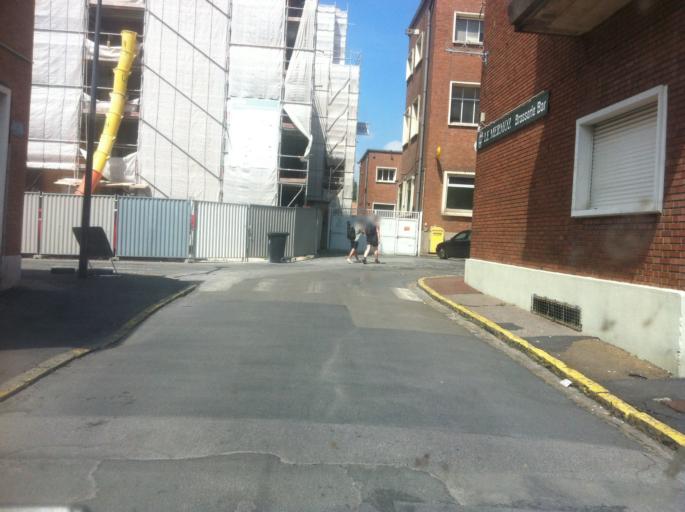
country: FR
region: Nord-Pas-de-Calais
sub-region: Departement du Nord
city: Maubeuge
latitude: 50.2781
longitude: 3.9726
